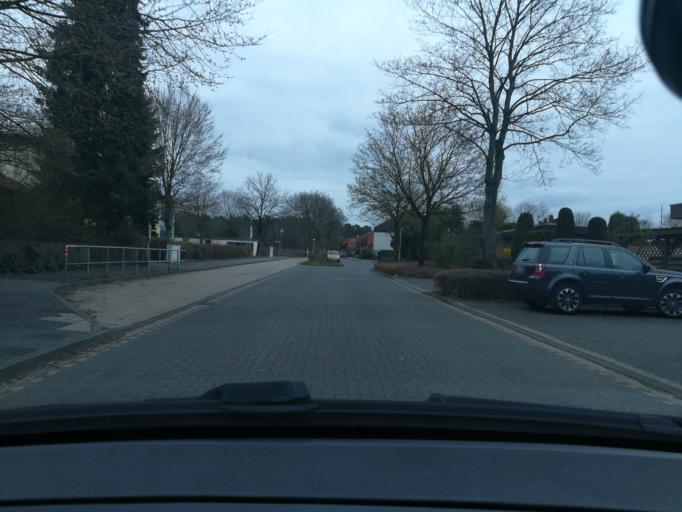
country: DE
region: North Rhine-Westphalia
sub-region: Regierungsbezirk Detmold
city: Oerlinghausen
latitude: 51.9358
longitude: 8.6359
